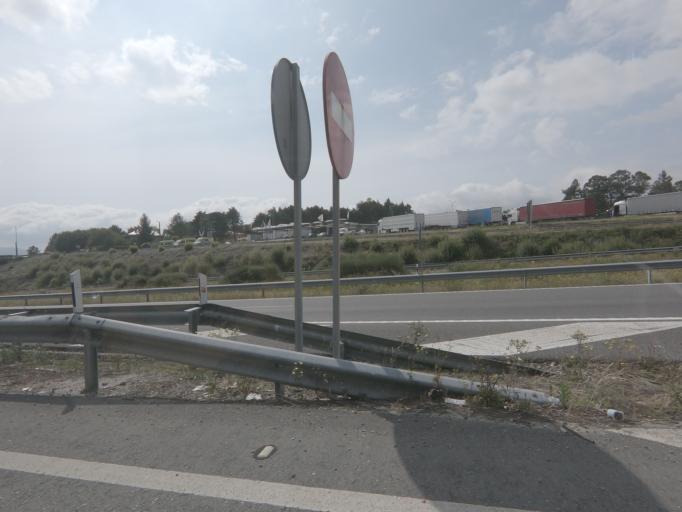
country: ES
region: Galicia
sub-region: Provincia de Ourense
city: Melon
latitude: 42.2067
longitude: -8.2660
